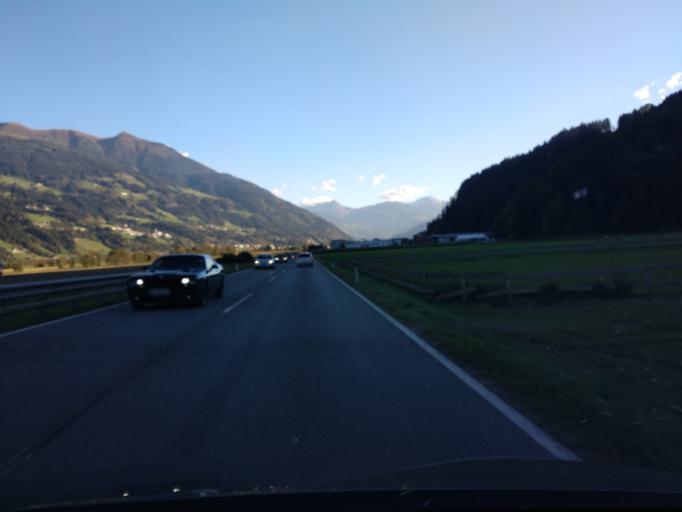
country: AT
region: Tyrol
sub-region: Politischer Bezirk Schwaz
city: Schlitters
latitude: 47.3728
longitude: 11.8461
